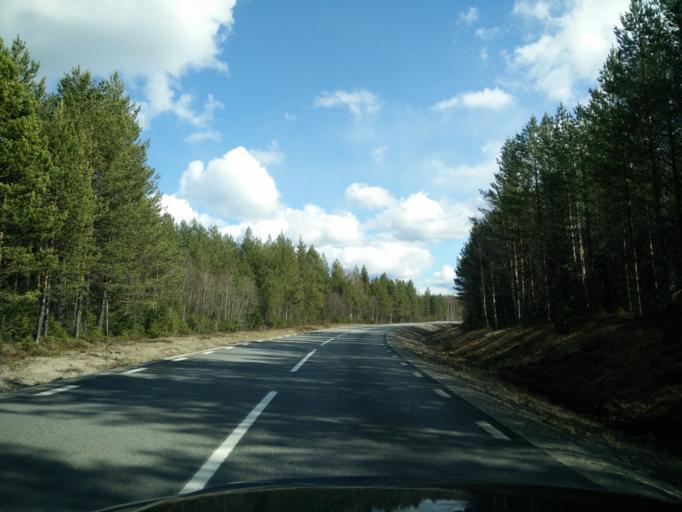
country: SE
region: Jaemtland
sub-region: Braecke Kommun
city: Braecke
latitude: 62.4515
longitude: 14.9751
